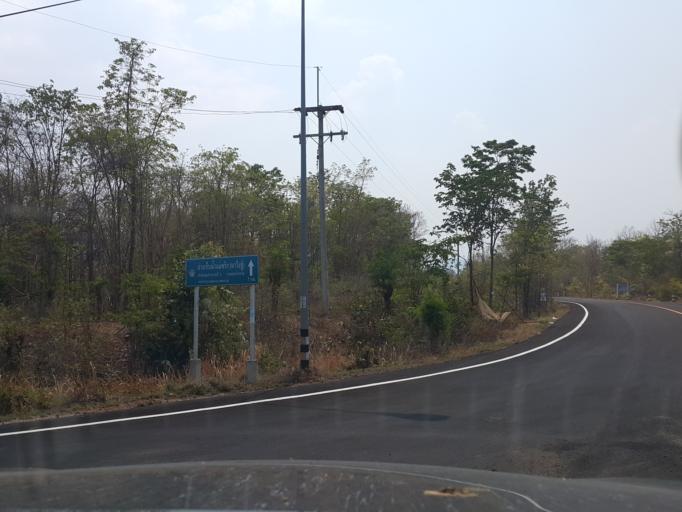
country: TH
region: Lampang
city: Mae Phrik
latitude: 17.4799
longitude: 99.1167
